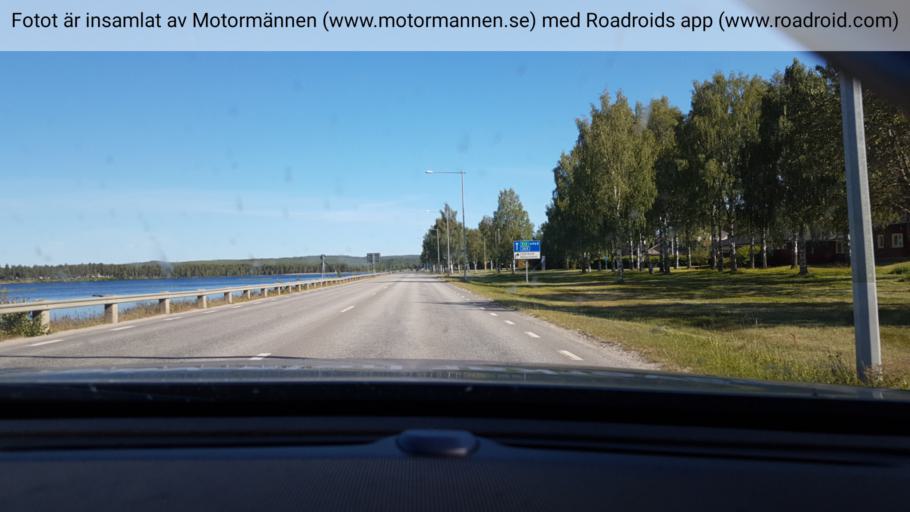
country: SE
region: Vaesterbotten
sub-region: Lycksele Kommun
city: Lycksele
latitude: 64.6018
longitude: 18.6748
